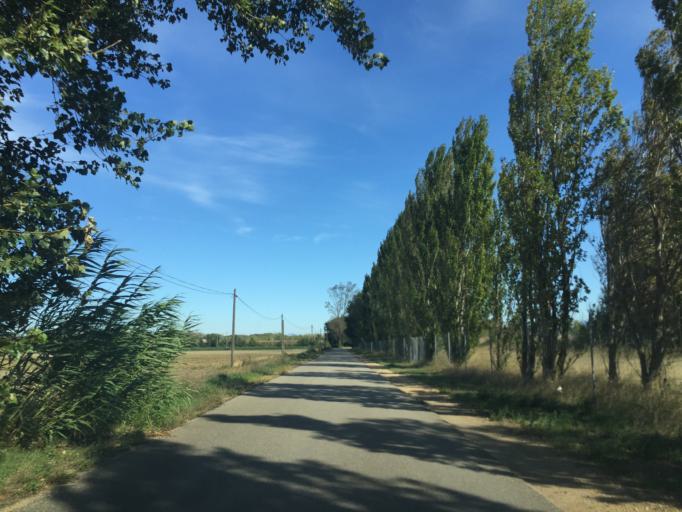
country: FR
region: Provence-Alpes-Cote d'Azur
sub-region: Departement du Vaucluse
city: Mornas
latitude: 44.1628
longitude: 4.7266
